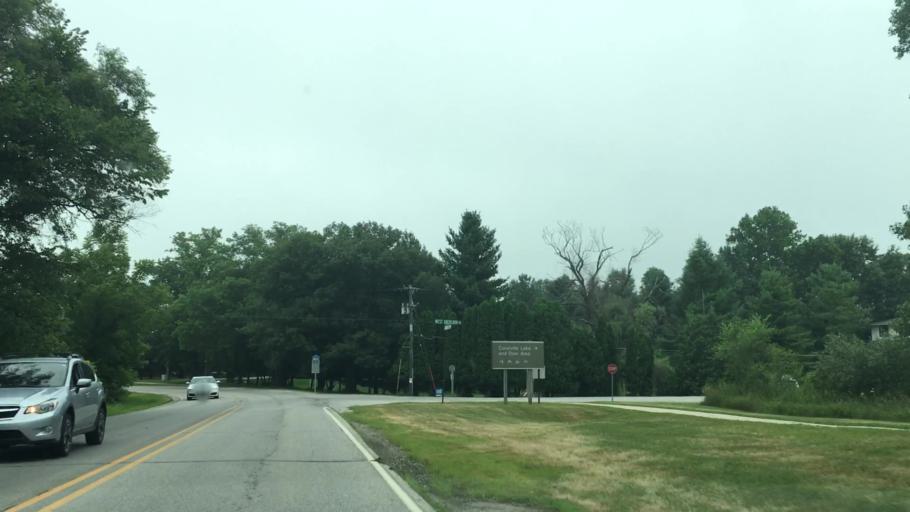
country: US
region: Iowa
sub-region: Johnson County
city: Coralville
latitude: 41.7191
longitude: -91.5537
